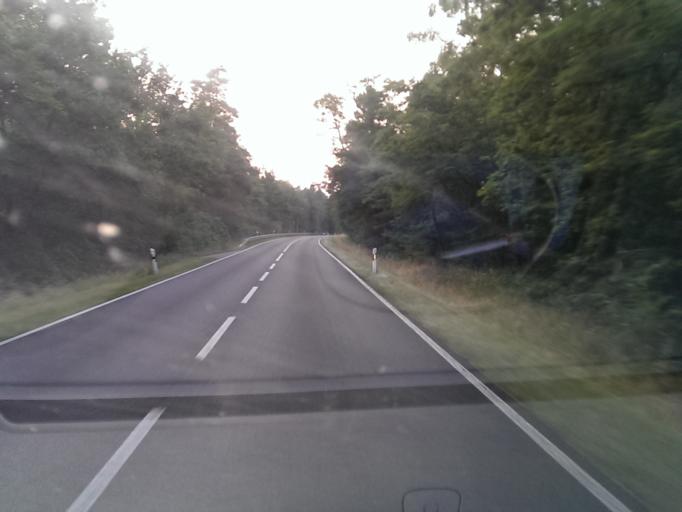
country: DE
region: Brandenburg
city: Golssen
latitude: 52.0066
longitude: 13.5535
